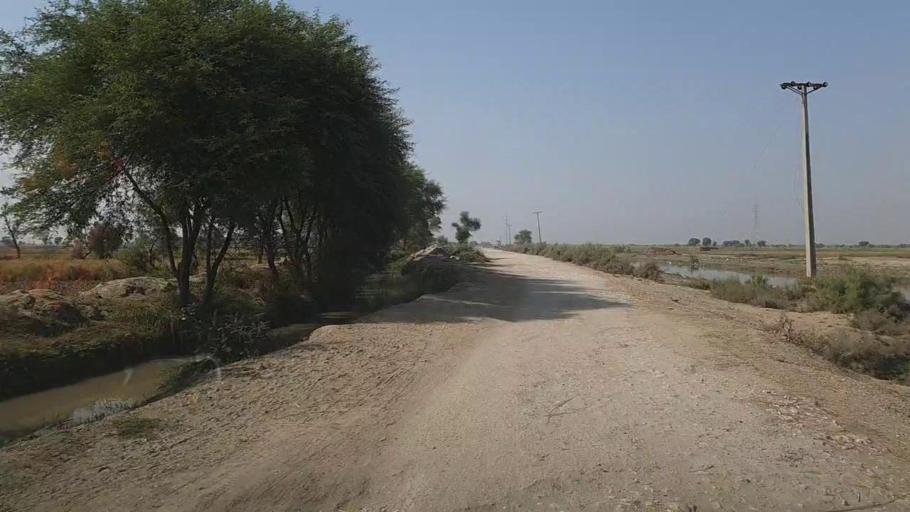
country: PK
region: Sindh
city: Kandhkot
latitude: 28.4067
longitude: 69.2523
